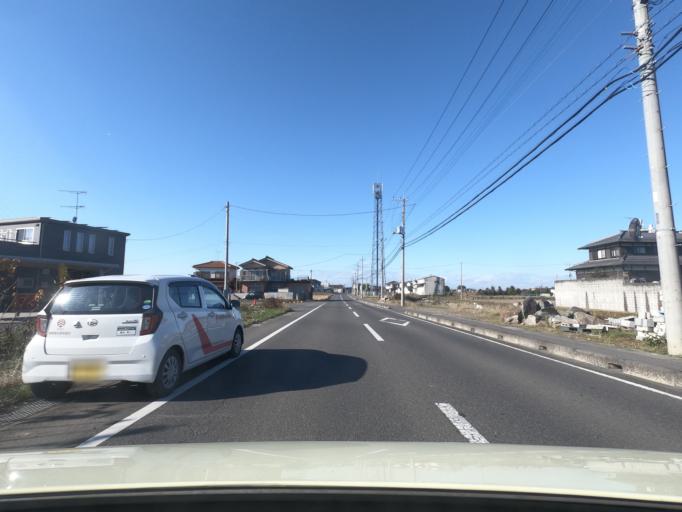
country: JP
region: Ibaraki
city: Ishige
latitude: 36.1751
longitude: 139.9788
